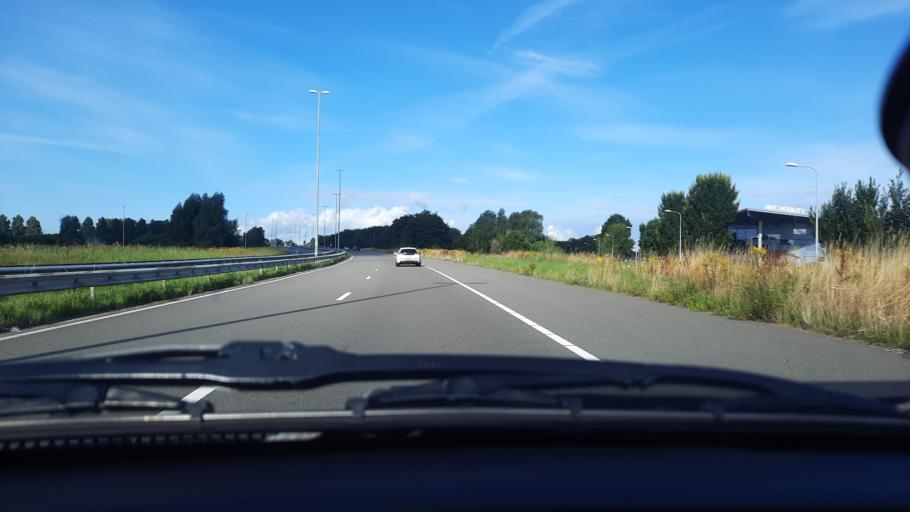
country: NL
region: Groningen
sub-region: Gemeente Haren
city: Haren
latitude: 53.2052
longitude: 6.6203
